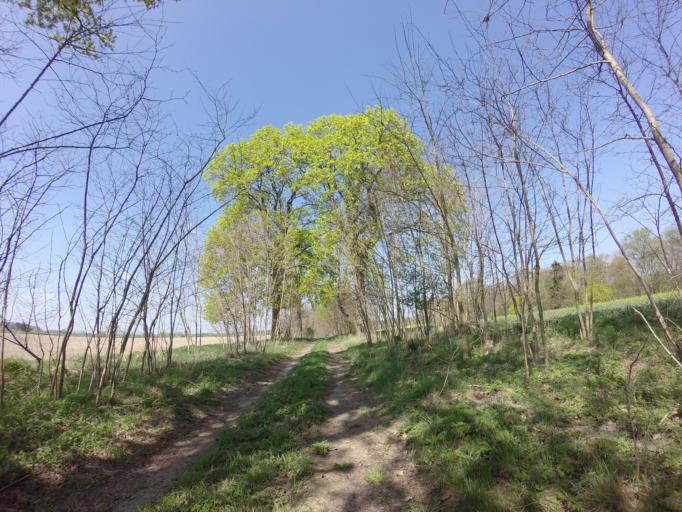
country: PL
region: West Pomeranian Voivodeship
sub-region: Powiat stargardzki
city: Suchan
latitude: 53.2173
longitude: 15.3491
